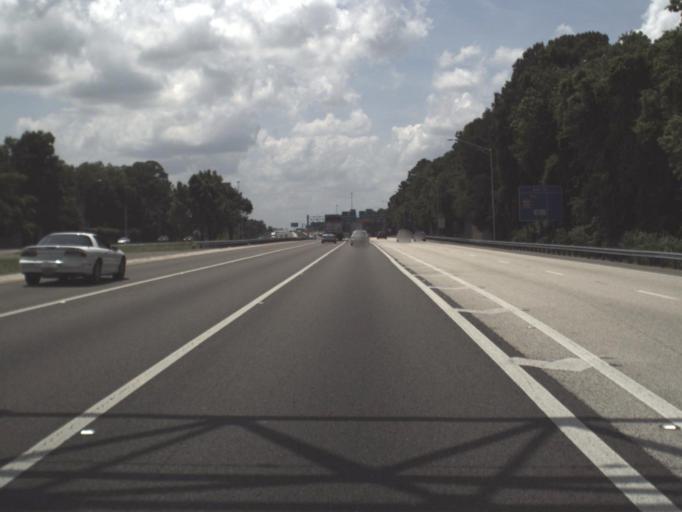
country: US
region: Florida
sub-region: Clay County
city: Orange Park
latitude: 30.1917
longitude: -81.6949
